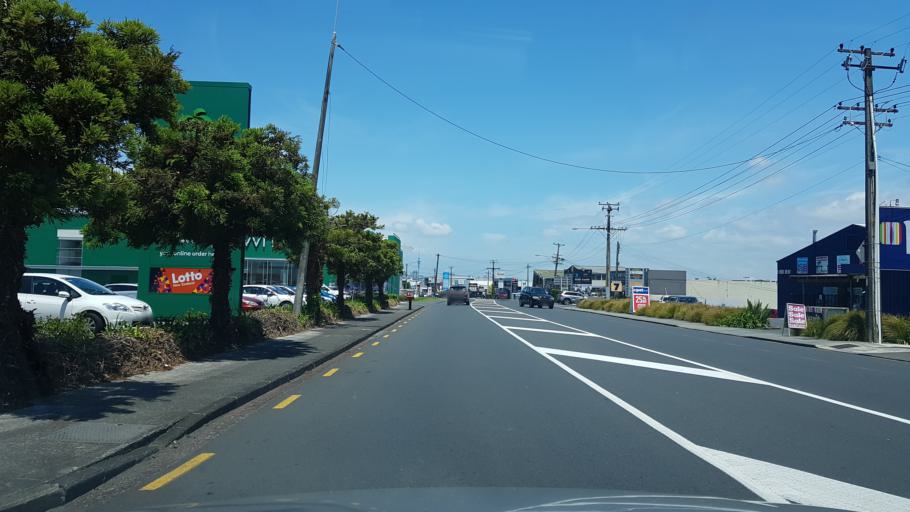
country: NZ
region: Auckland
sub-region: Auckland
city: North Shore
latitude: -36.7905
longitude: 174.7651
